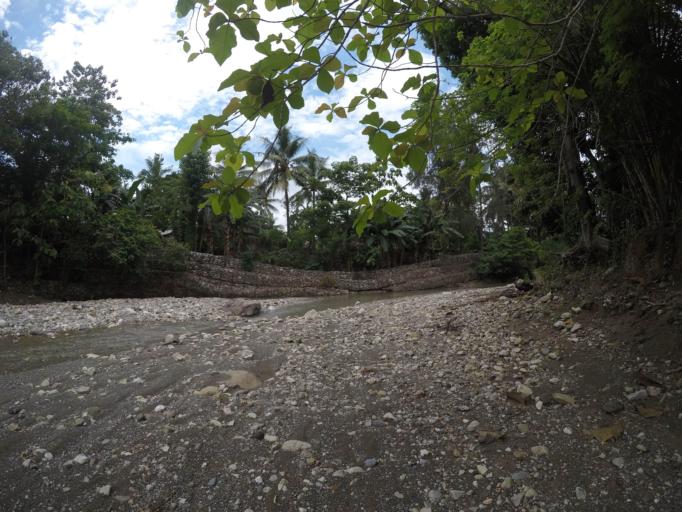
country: TL
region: Viqueque
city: Viqueque
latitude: -8.8588
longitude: 126.3626
